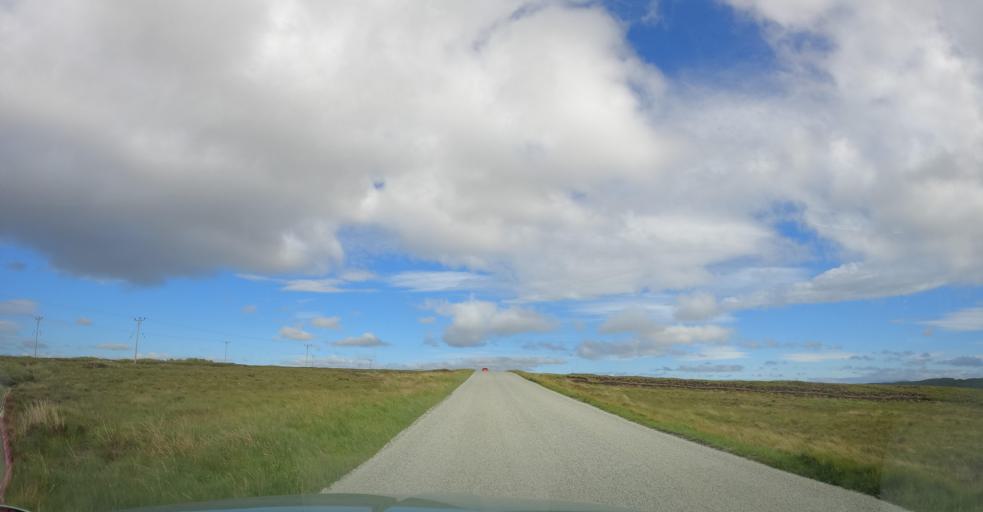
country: GB
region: Scotland
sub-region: Eilean Siar
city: Isle of Lewis
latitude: 58.1865
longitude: -6.6844
